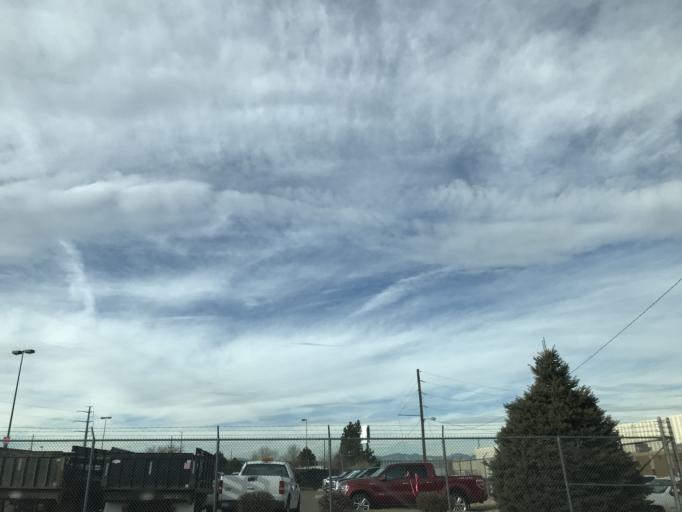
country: US
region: Colorado
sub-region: Adams County
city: Commerce City
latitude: 39.7749
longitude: -104.9055
